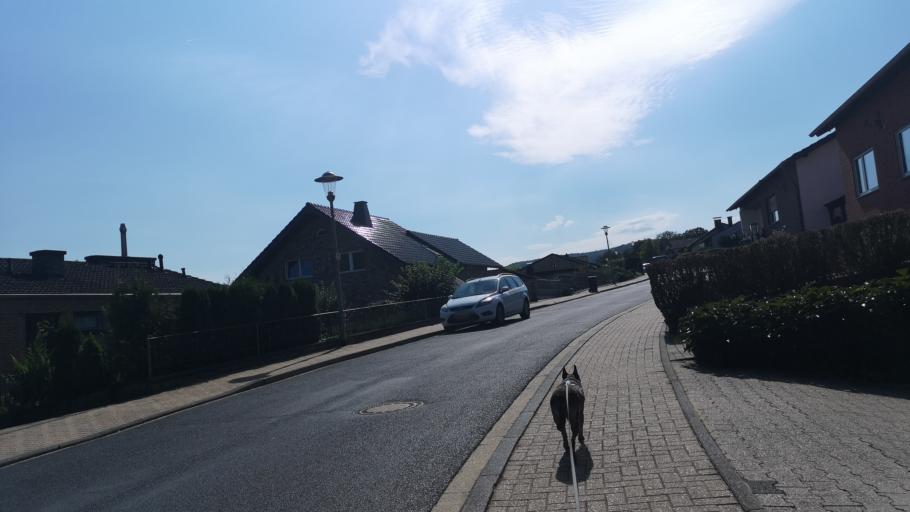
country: DE
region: North Rhine-Westphalia
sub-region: Regierungsbezirk Koln
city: Nideggen
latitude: 50.6726
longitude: 6.4756
